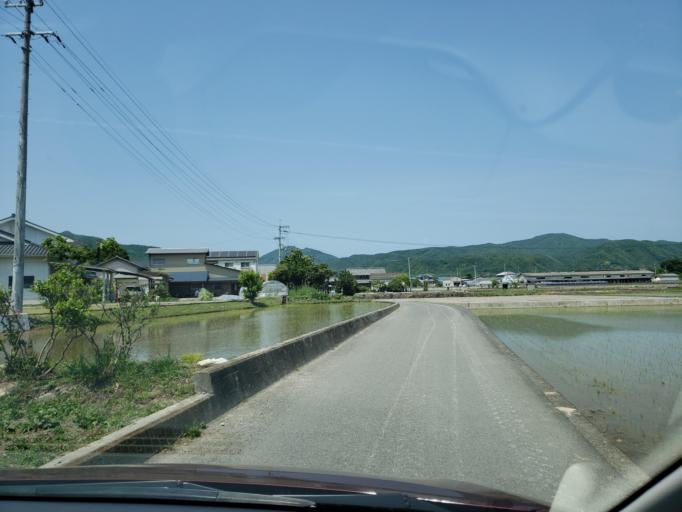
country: JP
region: Tokushima
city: Kamojimacho-jogejima
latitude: 34.0879
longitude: 134.2680
